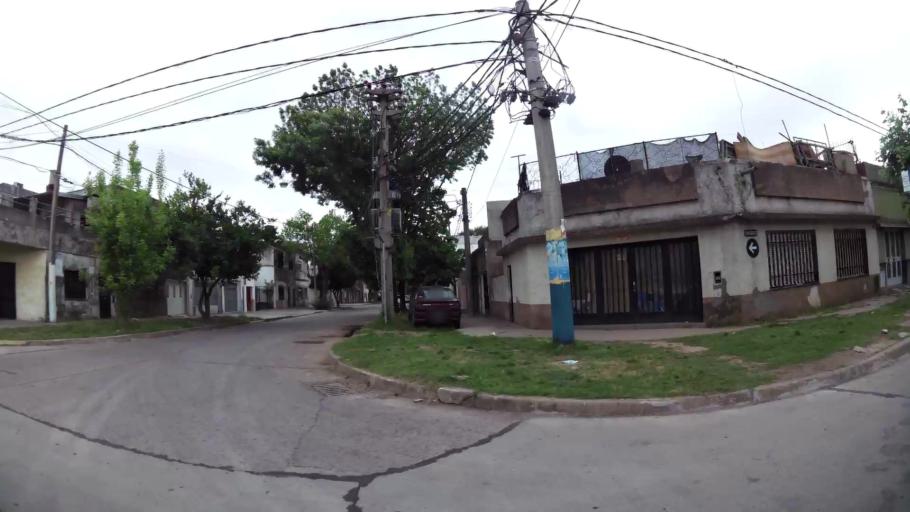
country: AR
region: Santa Fe
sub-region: Departamento de Rosario
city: Rosario
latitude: -32.9875
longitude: -60.6529
